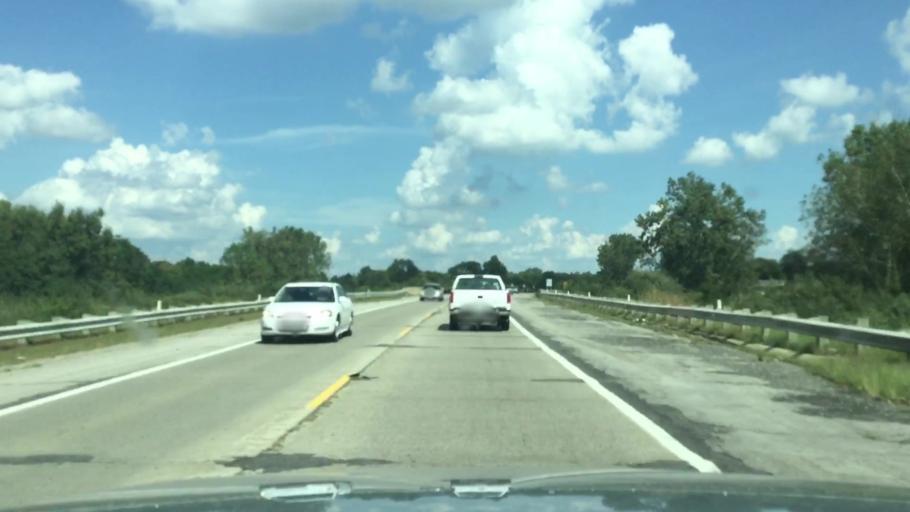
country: US
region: Michigan
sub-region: Washtenaw County
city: Saline
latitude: 42.1915
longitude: -83.7242
